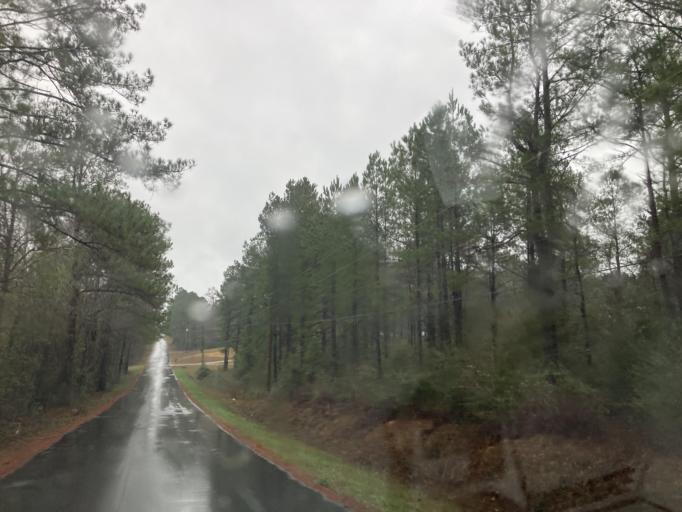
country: US
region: Mississippi
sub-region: Forrest County
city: Rawls Springs
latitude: 31.4684
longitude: -89.3822
